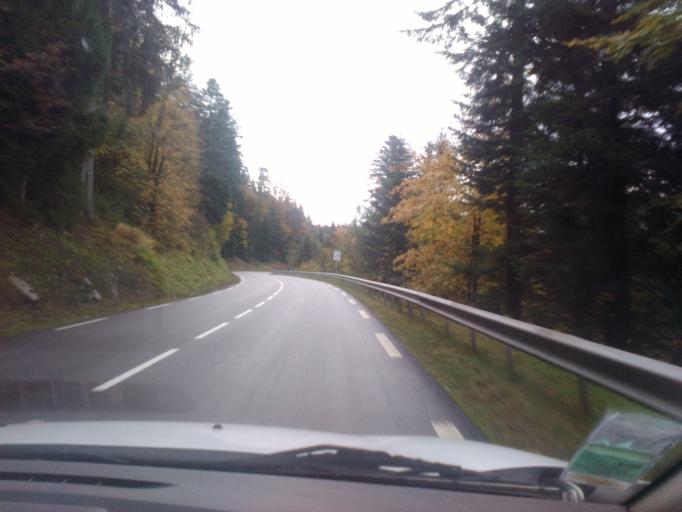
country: FR
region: Lorraine
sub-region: Departement des Vosges
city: Xonrupt-Longemer
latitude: 48.1091
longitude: 6.9084
